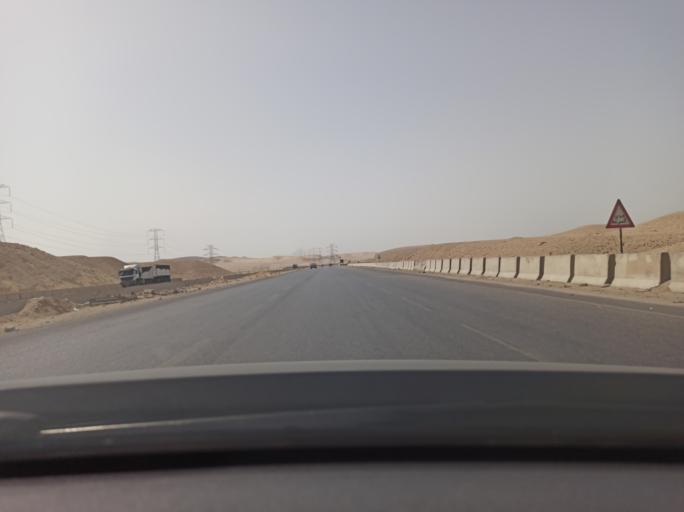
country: EG
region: Al Jizah
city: As Saff
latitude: 29.5339
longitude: 31.3874
